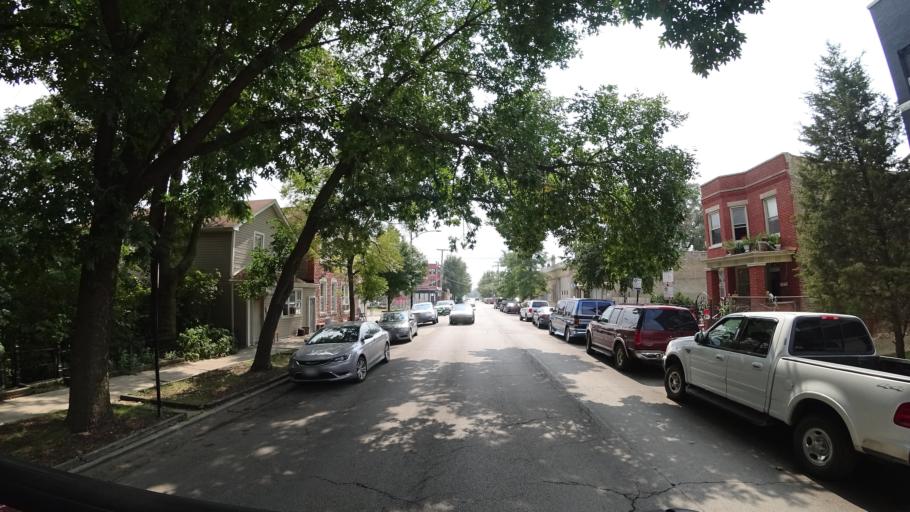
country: US
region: Illinois
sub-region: Cook County
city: Chicago
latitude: 41.8493
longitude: -87.6782
